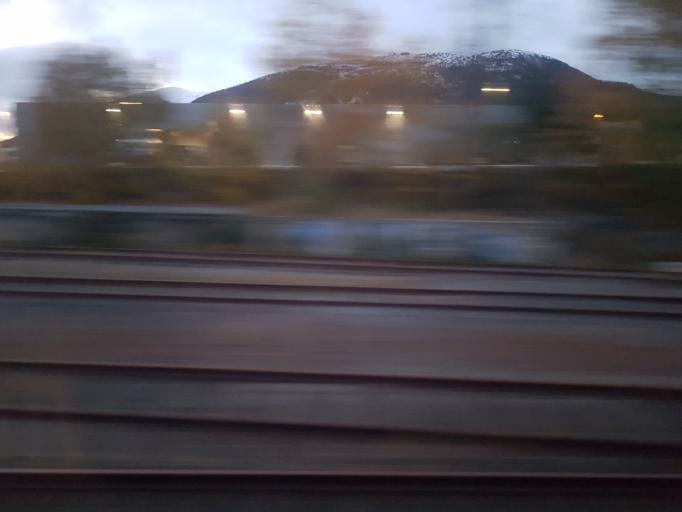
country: NO
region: Sor-Trondelag
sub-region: Oppdal
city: Oppdal
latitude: 62.5962
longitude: 9.6985
